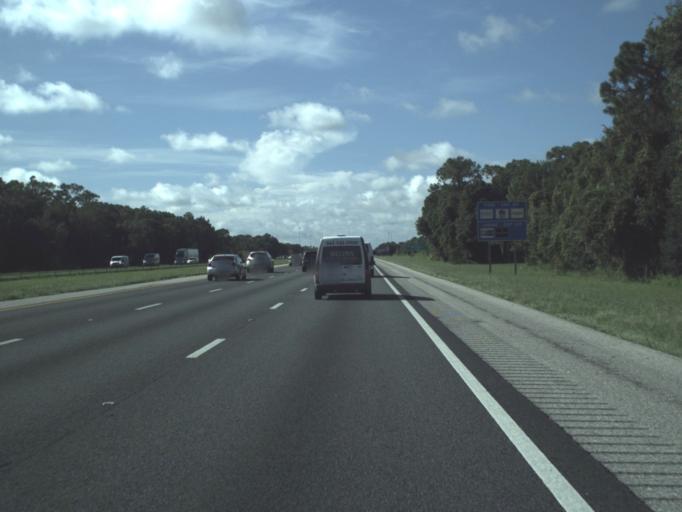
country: US
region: Florida
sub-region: Manatee County
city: Samoset
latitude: 27.4563
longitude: -82.4594
